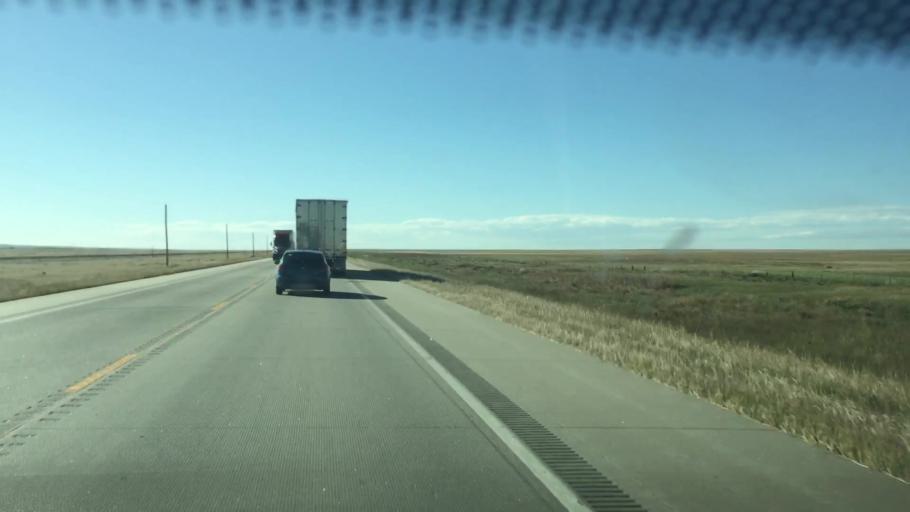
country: US
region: Colorado
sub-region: Kiowa County
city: Eads
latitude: 38.8309
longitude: -103.0433
